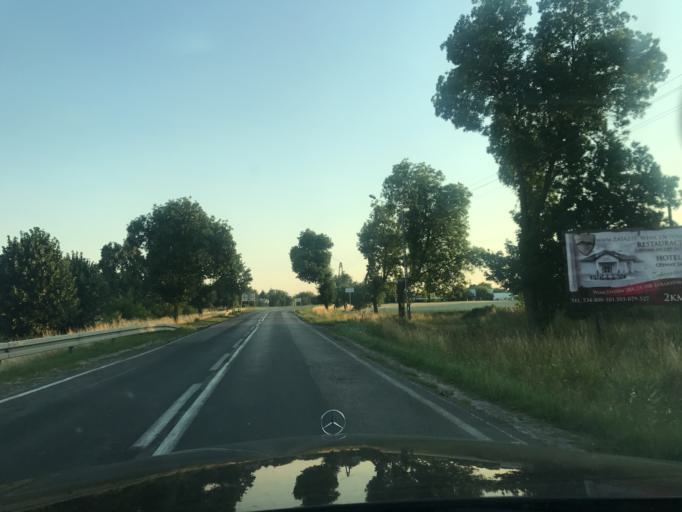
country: PL
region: Lublin Voivodeship
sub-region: Powiat lubartowski
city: Lubartow
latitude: 51.4755
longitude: 22.6114
